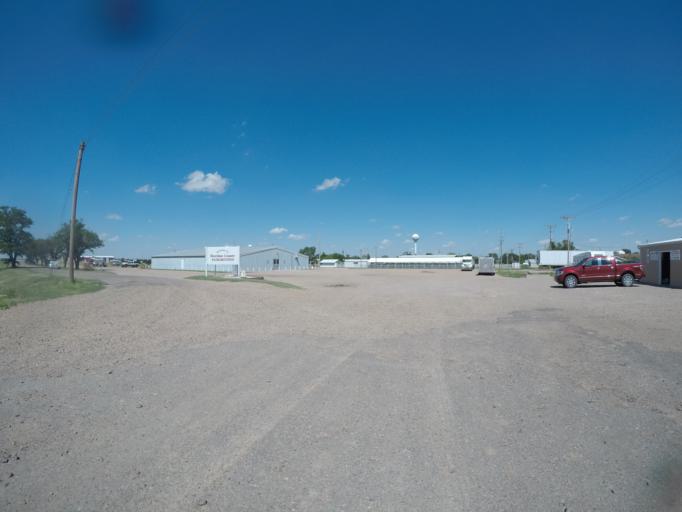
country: US
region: Kansas
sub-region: Sheridan County
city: Hoxie
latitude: 39.3585
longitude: -100.4417
